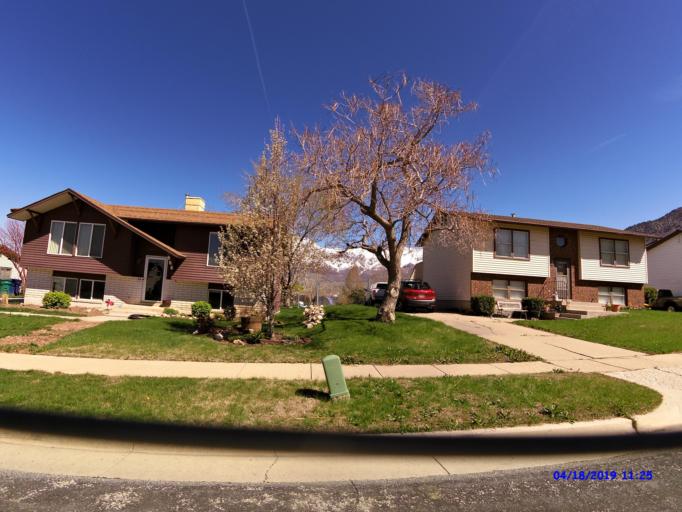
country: US
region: Utah
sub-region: Weber County
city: North Ogden
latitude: 41.2787
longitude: -111.9562
